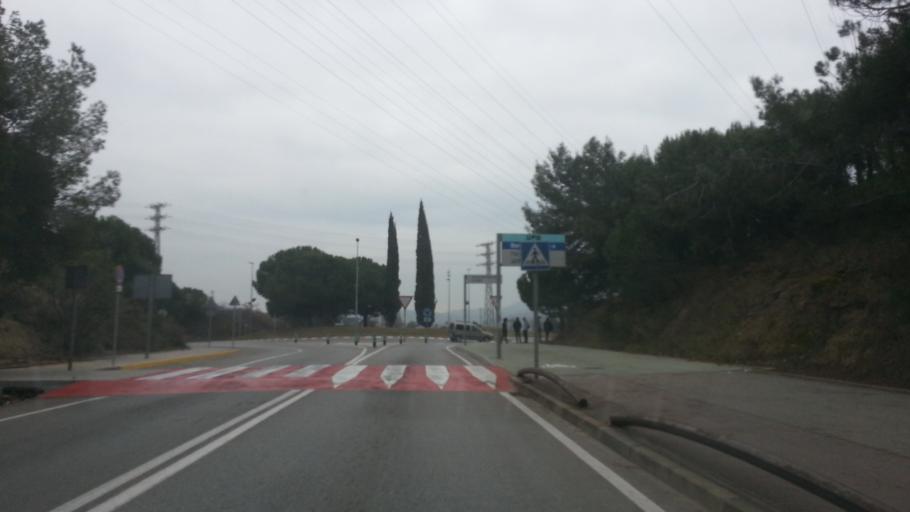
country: ES
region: Catalonia
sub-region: Provincia de Barcelona
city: Barbera del Valles
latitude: 41.5001
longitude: 2.1139
